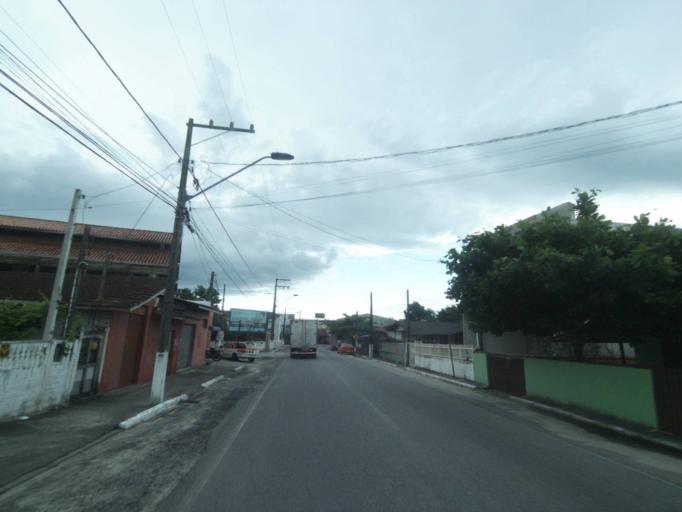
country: BR
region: Parana
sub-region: Guaratuba
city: Guaratuba
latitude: -25.8177
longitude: -48.5387
